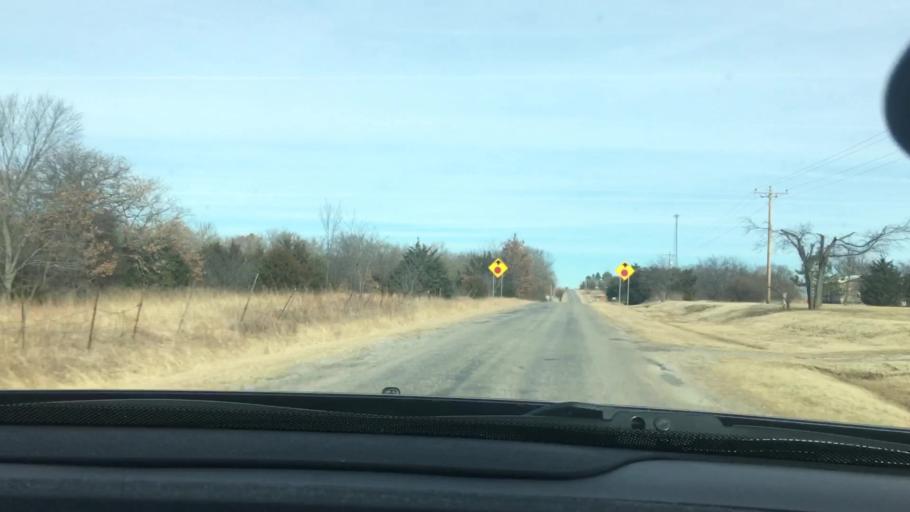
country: US
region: Oklahoma
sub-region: Garvin County
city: Wynnewood
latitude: 34.6496
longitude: -97.2476
